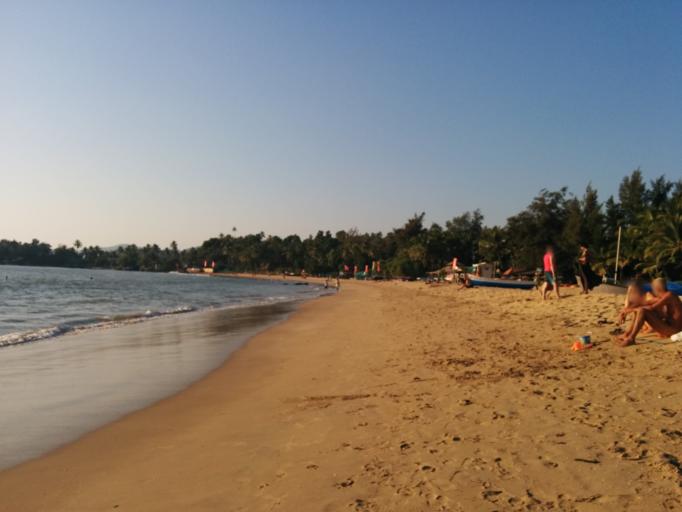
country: IN
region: Karnataka
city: Canacona
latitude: 14.9975
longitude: 74.0334
